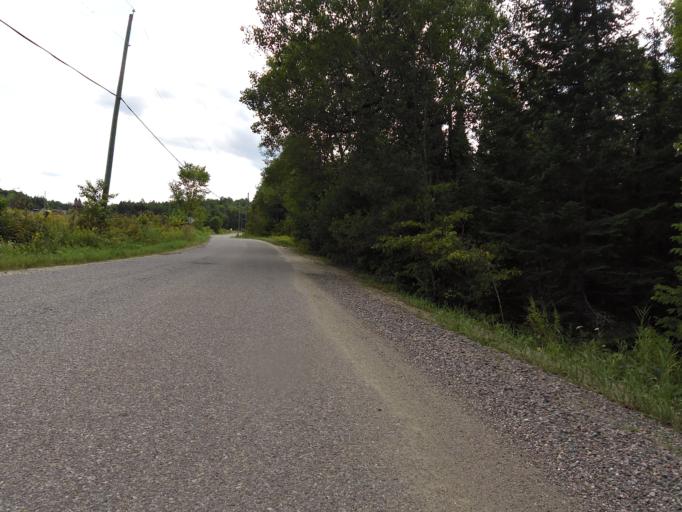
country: CA
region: Quebec
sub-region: Outaouais
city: Wakefield
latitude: 45.8070
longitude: -75.9847
